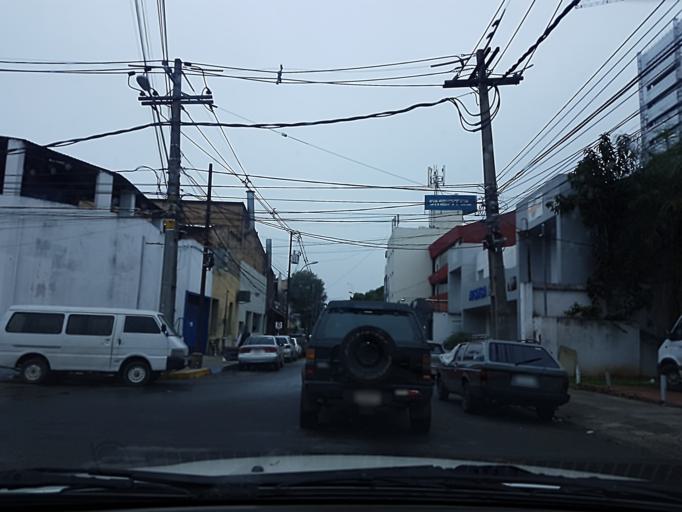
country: PY
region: Asuncion
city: Asuncion
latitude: -25.2958
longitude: -57.5786
